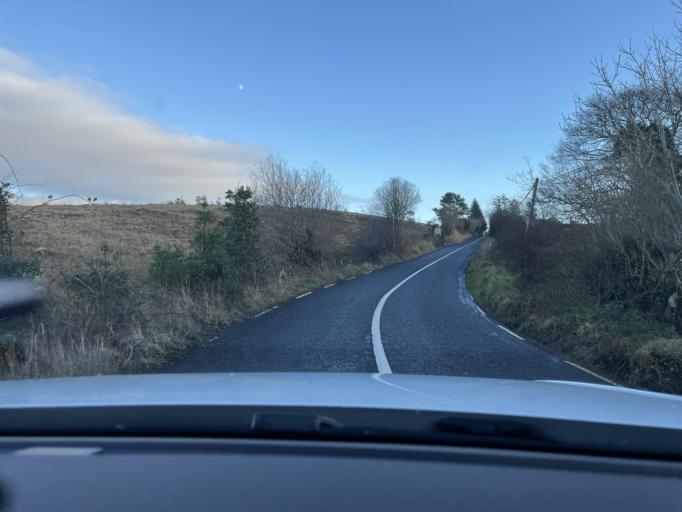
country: IE
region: Connaught
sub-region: County Leitrim
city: Manorhamilton
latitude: 54.1969
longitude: -7.9283
